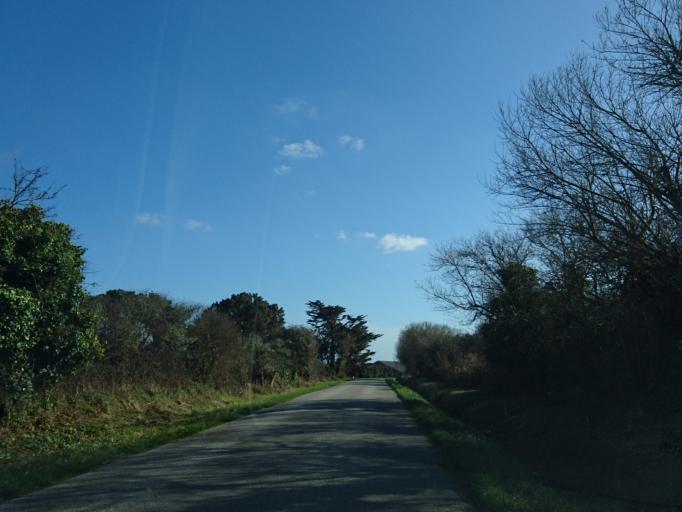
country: FR
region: Brittany
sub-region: Departement du Finistere
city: Roscanvel
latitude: 48.3007
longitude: -4.5628
